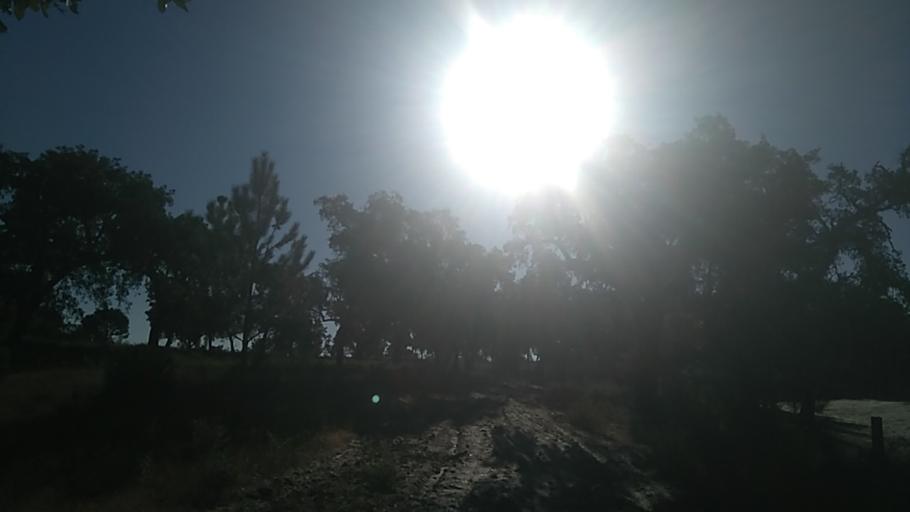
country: PT
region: Santarem
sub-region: Coruche
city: Coruche
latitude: 38.8605
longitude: -8.5208
